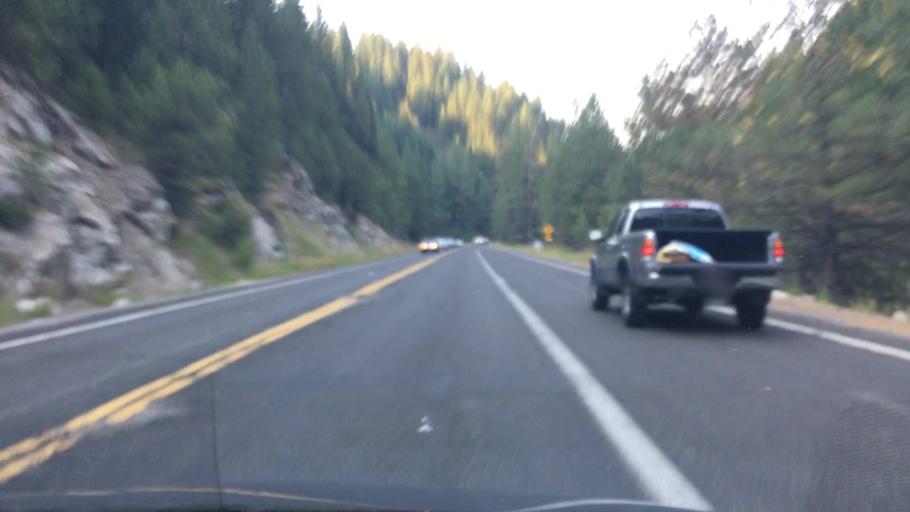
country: US
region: Idaho
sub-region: Valley County
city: Cascade
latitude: 44.2521
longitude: -116.0870
